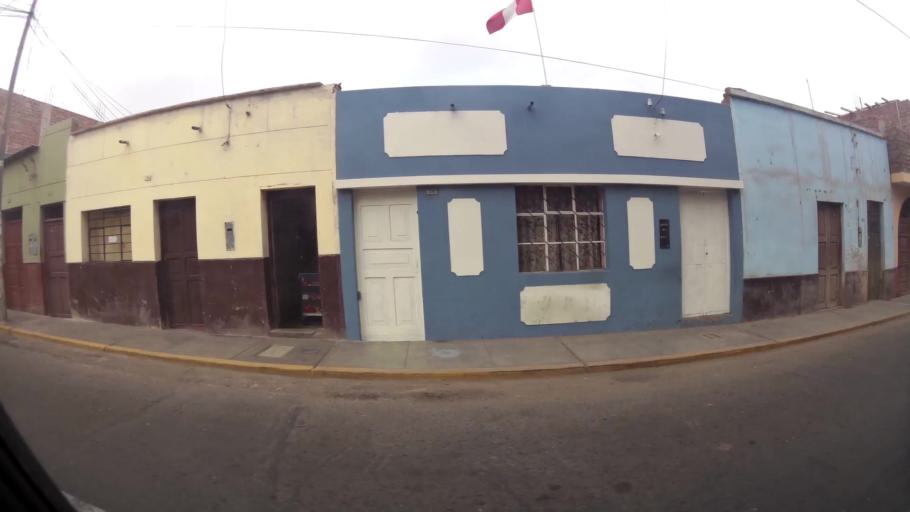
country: PE
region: La Libertad
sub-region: Provincia de Trujillo
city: Trujillo
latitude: -8.0983
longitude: -79.0166
